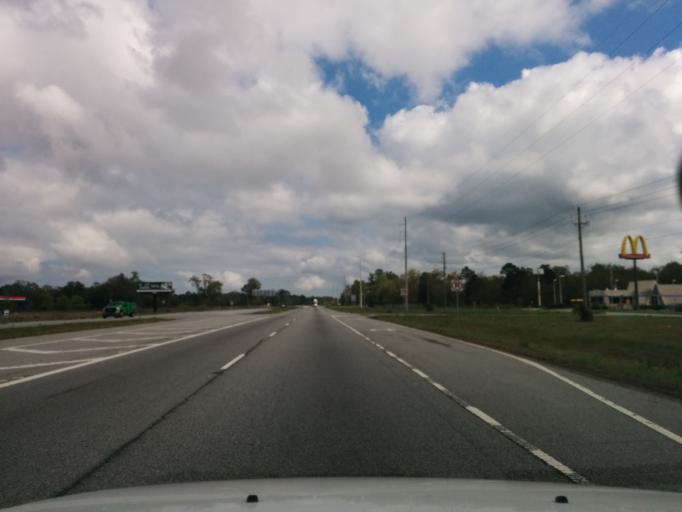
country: US
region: Georgia
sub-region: Glynn County
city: Brunswick
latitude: 31.1350
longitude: -81.5686
